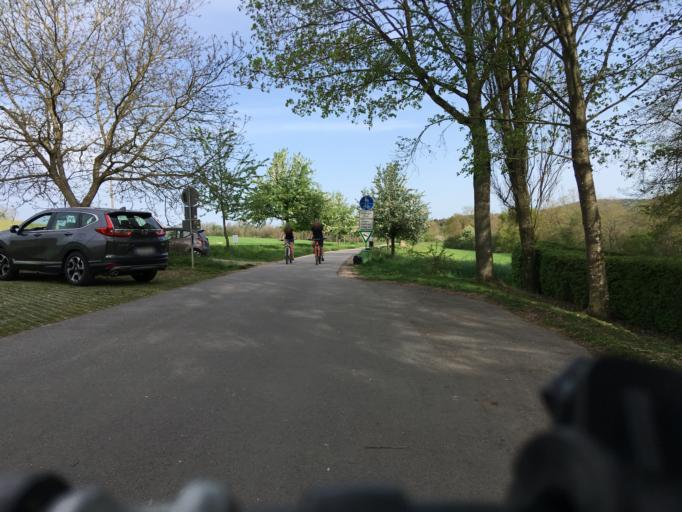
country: DE
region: Baden-Wuerttemberg
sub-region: Freiburg Region
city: Gailingen
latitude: 47.6887
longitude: 8.7631
